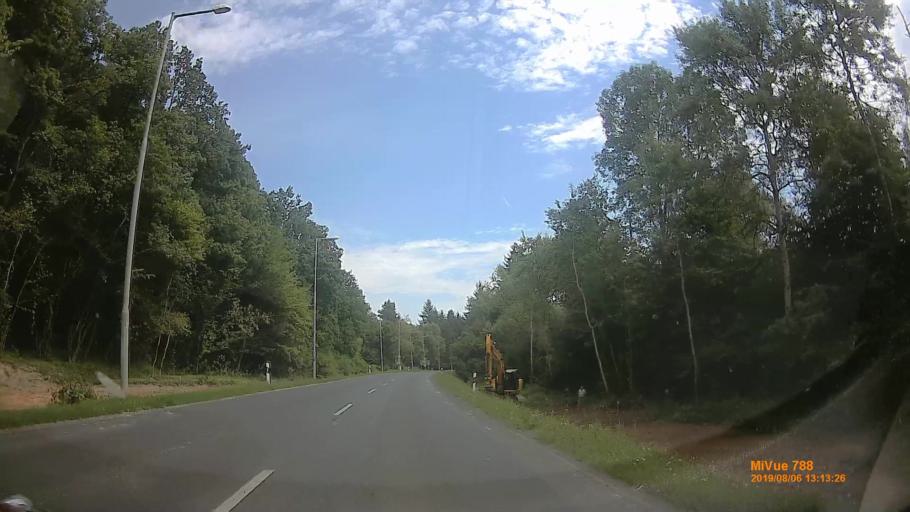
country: AT
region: Burgenland
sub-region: Politischer Bezirk Oberpullendorf
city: Mannersdorf an der Rabnitz
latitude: 47.4070
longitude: 16.5231
